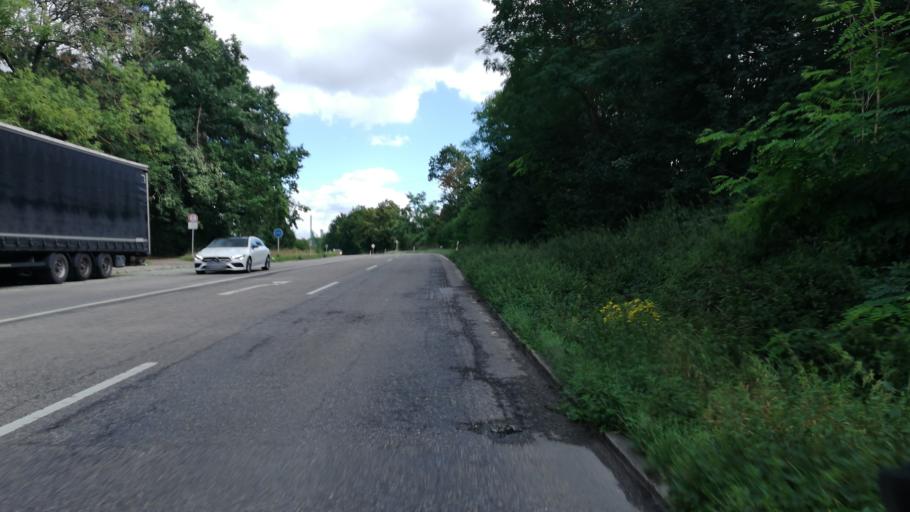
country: DE
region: Baden-Wuerttemberg
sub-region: Regierungsbezirk Stuttgart
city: Waiblingen
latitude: 48.8653
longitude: 9.2790
